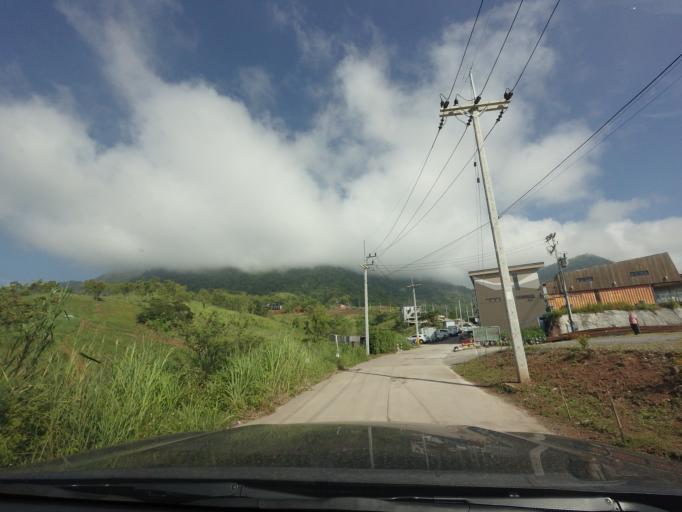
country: TH
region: Phetchabun
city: Khao Kho
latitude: 16.7943
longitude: 101.0418
